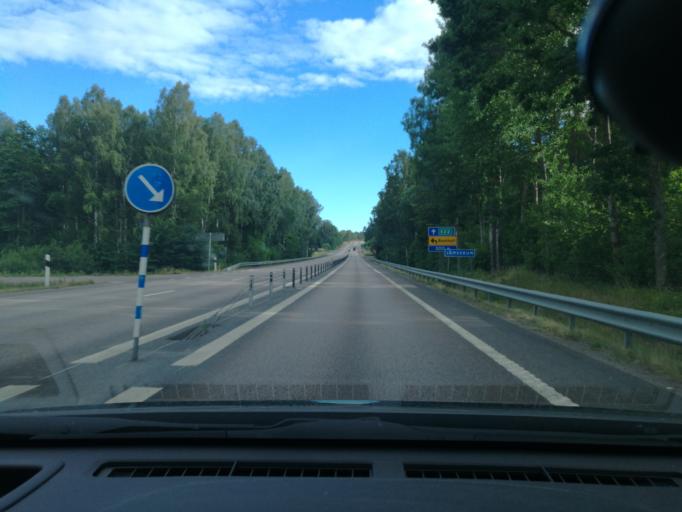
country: SE
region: Kalmar
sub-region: Oskarshamns Kommun
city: Oskarshamn
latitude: 57.4157
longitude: 16.4817
